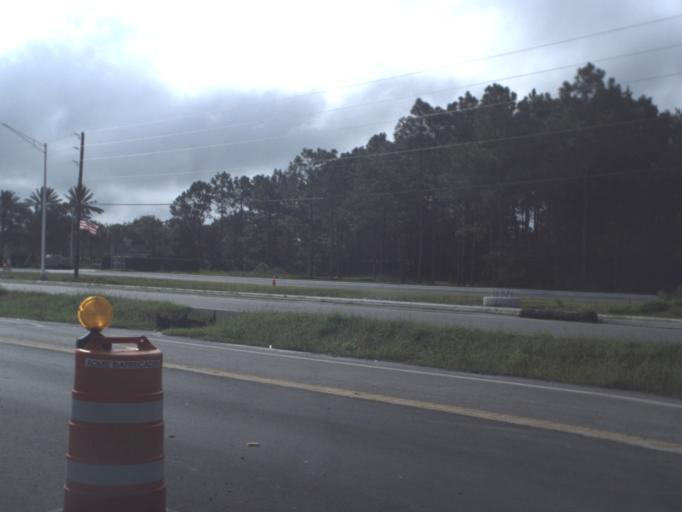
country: US
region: Florida
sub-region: Pasco County
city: San Antonio
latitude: 28.3248
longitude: -82.3302
